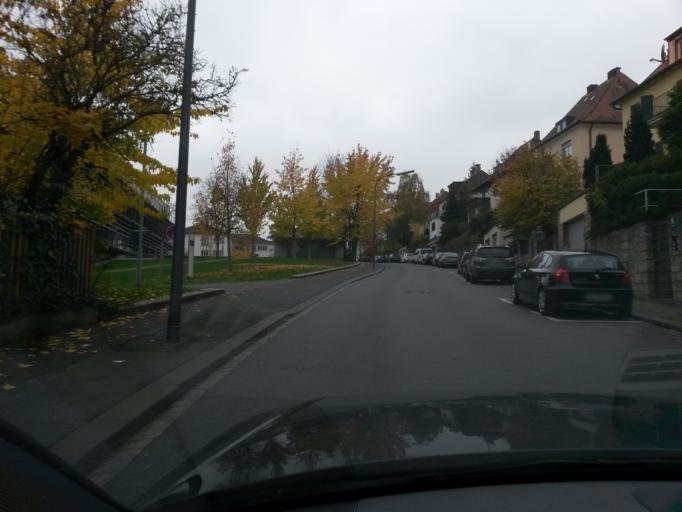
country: DE
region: Bavaria
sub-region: Regierungsbezirk Unterfranken
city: Wuerzburg
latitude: 49.8053
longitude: 9.9596
